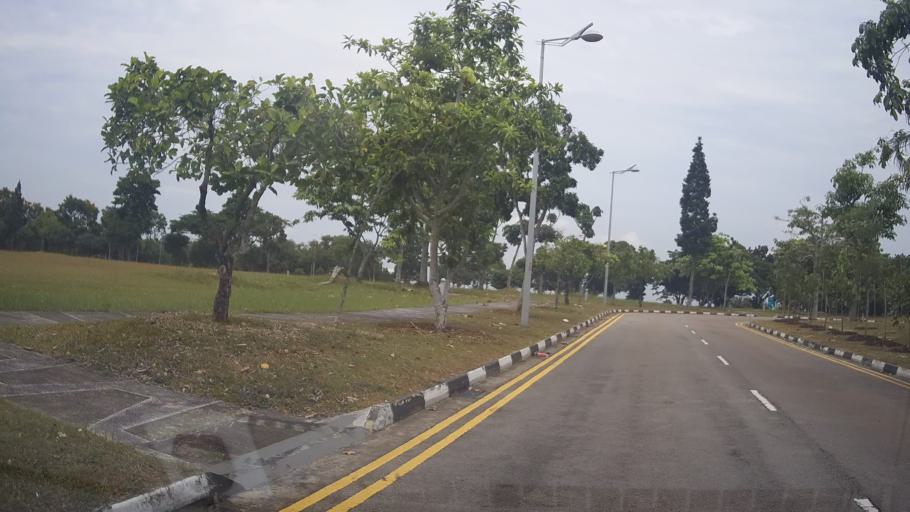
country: SG
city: Singapore
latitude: 1.3399
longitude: 103.9696
